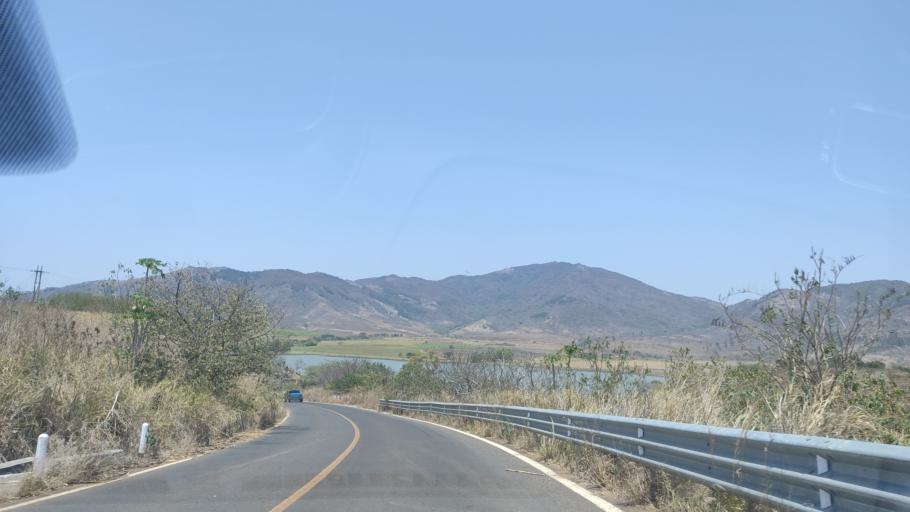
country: MX
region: Nayarit
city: Puga
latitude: 21.6051
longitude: -104.7387
